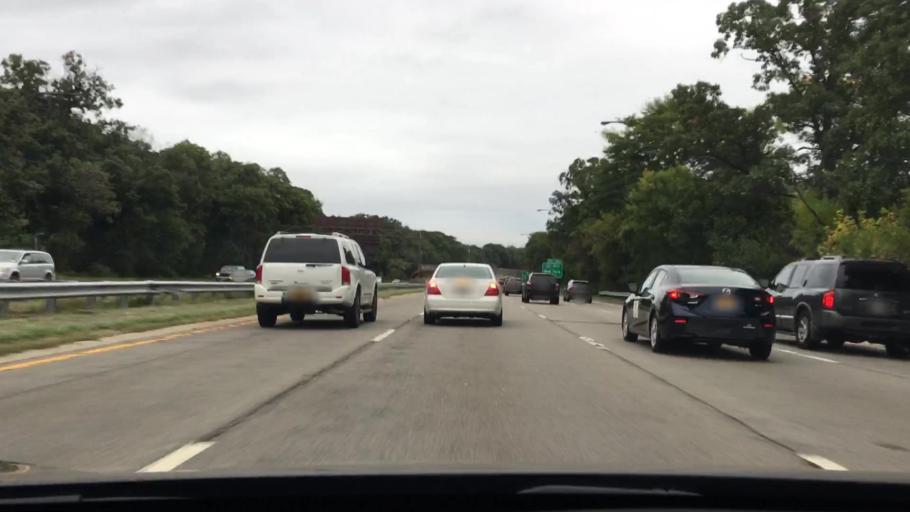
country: US
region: New York
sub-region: Nassau County
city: East Williston
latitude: 40.7689
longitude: -73.6254
